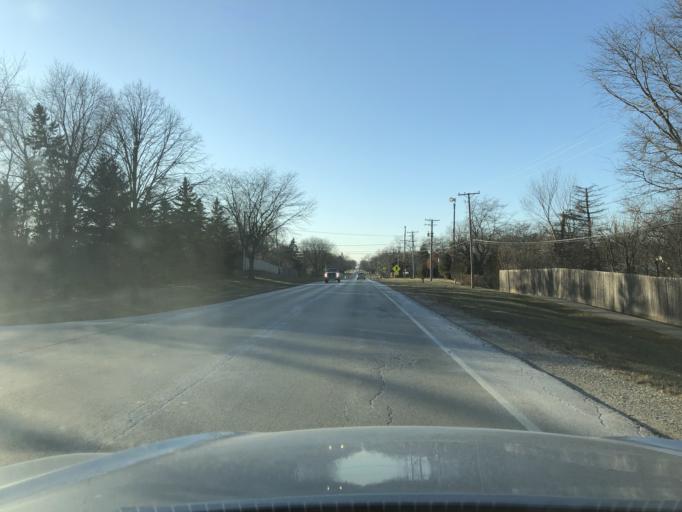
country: US
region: Illinois
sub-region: Cook County
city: Barrington
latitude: 42.1542
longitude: -88.1099
